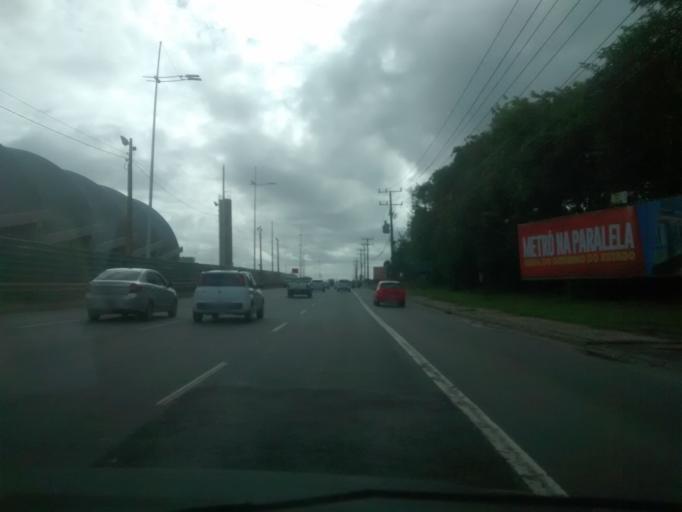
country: BR
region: Bahia
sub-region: Salvador
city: Salvador
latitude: -12.9569
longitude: -38.4294
